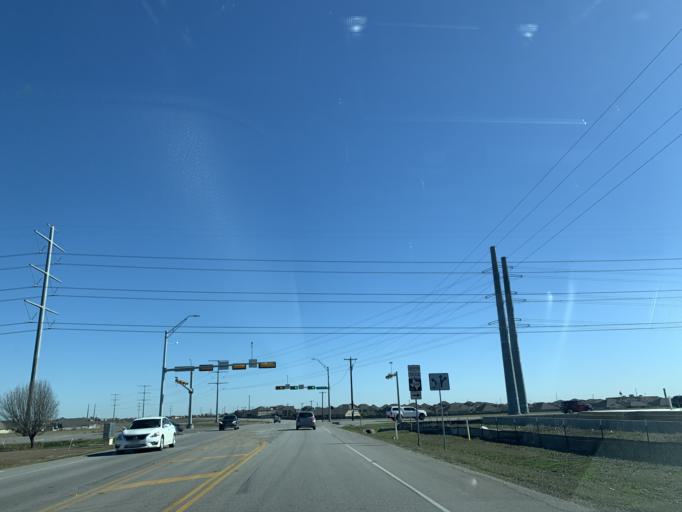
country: US
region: Texas
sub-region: Williamson County
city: Hutto
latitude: 30.5572
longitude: -97.5598
